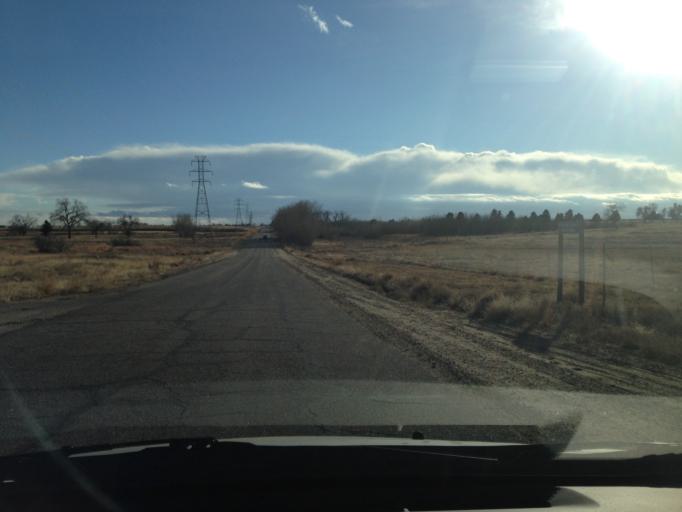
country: US
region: Colorado
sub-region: Adams County
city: Derby
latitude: 39.8224
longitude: -104.8658
